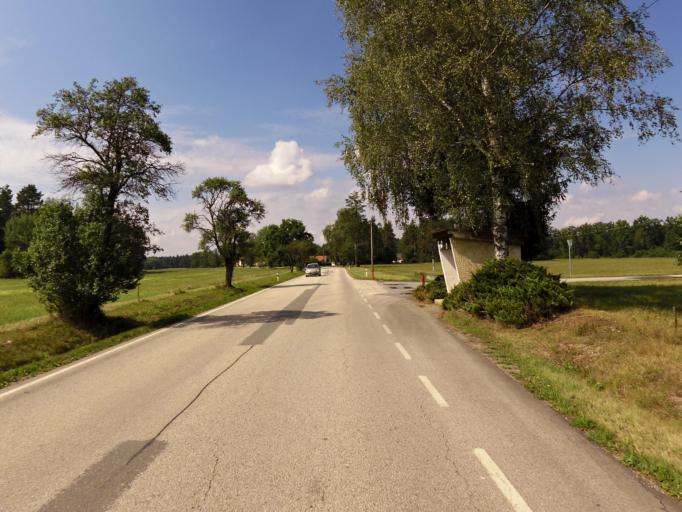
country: CZ
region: Jihocesky
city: Chlum u Trebone
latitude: 48.9513
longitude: 14.9057
